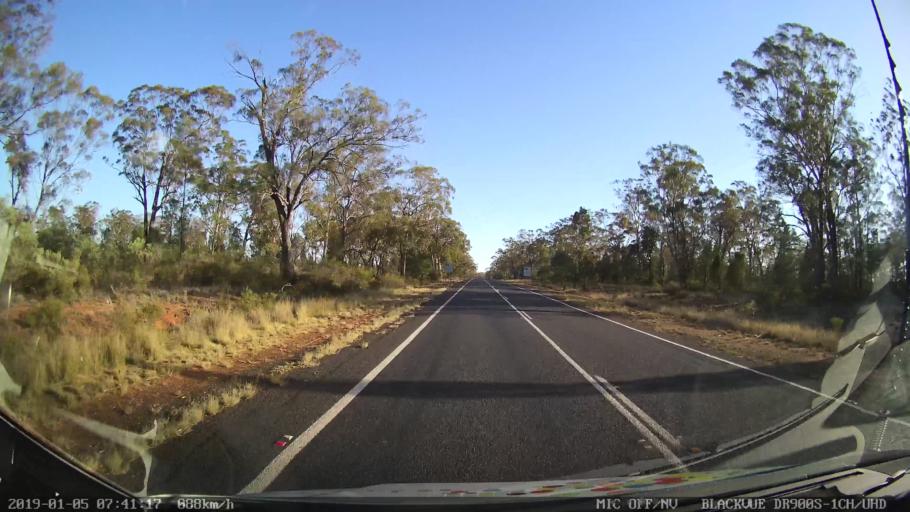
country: AU
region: New South Wales
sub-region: Gilgandra
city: Gilgandra
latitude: -31.9128
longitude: 148.6202
